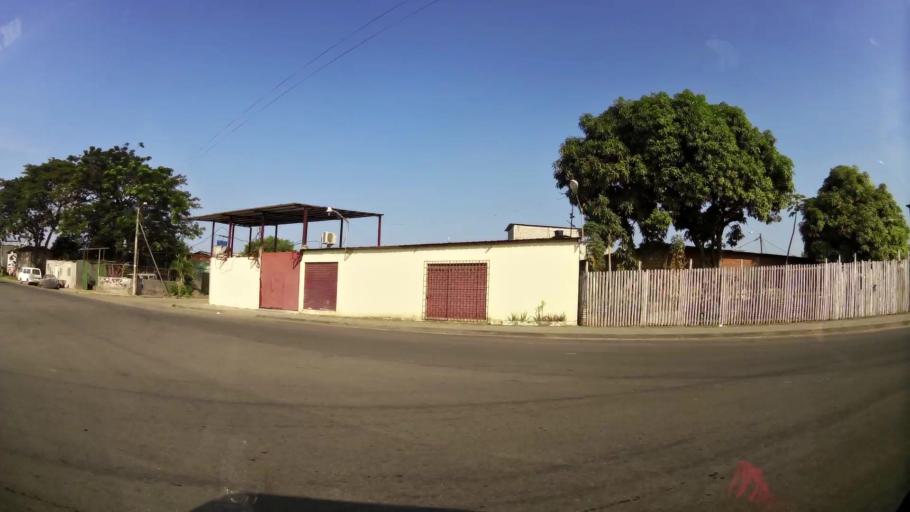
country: EC
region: Guayas
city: Eloy Alfaro
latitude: -2.1854
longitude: -79.8495
